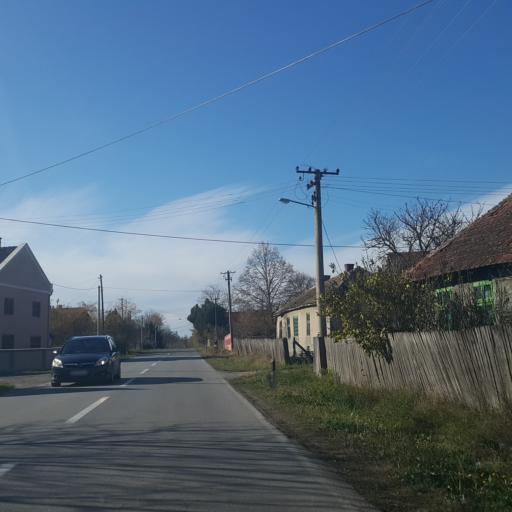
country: RS
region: Central Serbia
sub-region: Sumadijski Okrug
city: Topola
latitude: 44.2522
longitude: 20.7967
